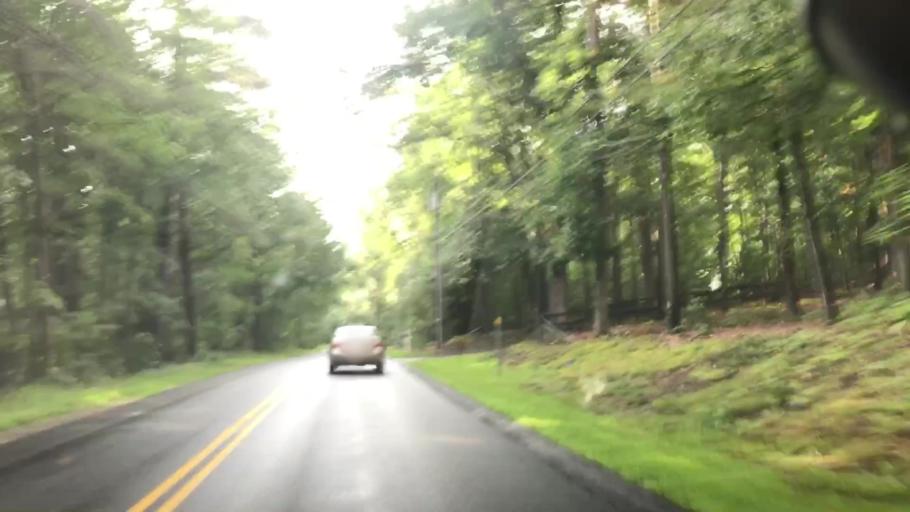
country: US
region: New Hampshire
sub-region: Hillsborough County
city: Milford
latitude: 42.8419
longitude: -71.6048
